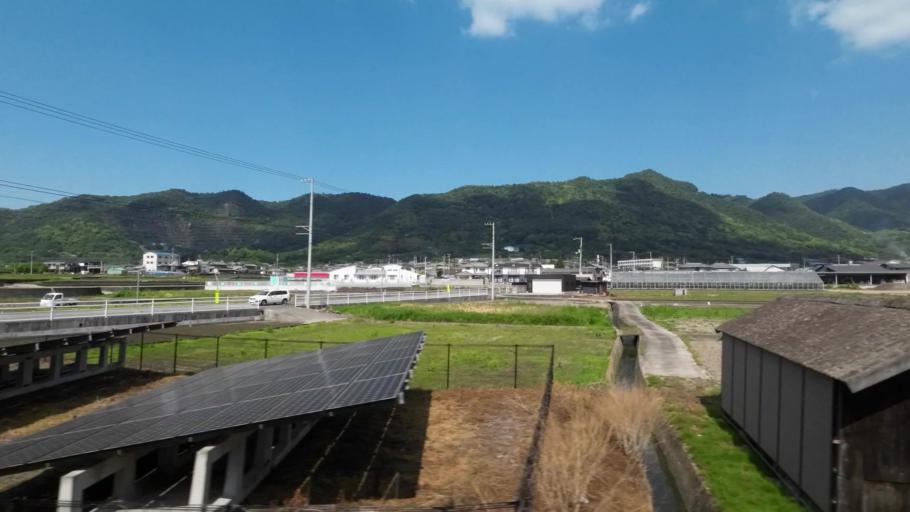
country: JP
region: Kagawa
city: Kan'onjicho
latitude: 34.1515
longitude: 133.6873
